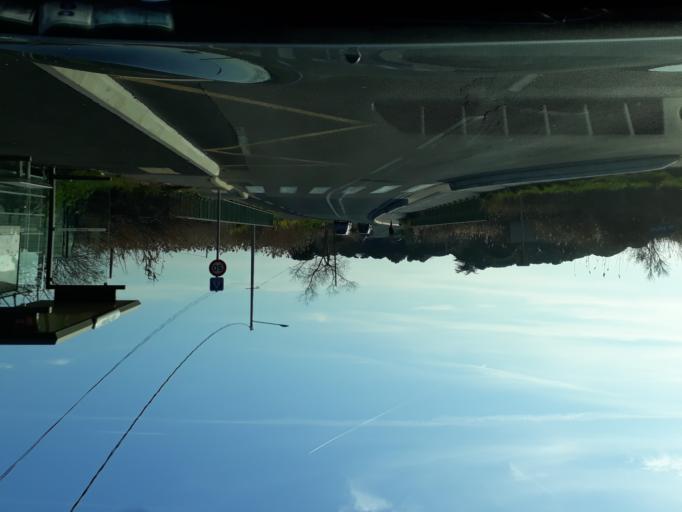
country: FR
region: Languedoc-Roussillon
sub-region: Departement de l'Herault
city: Marseillan
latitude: 43.3209
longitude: 3.5347
